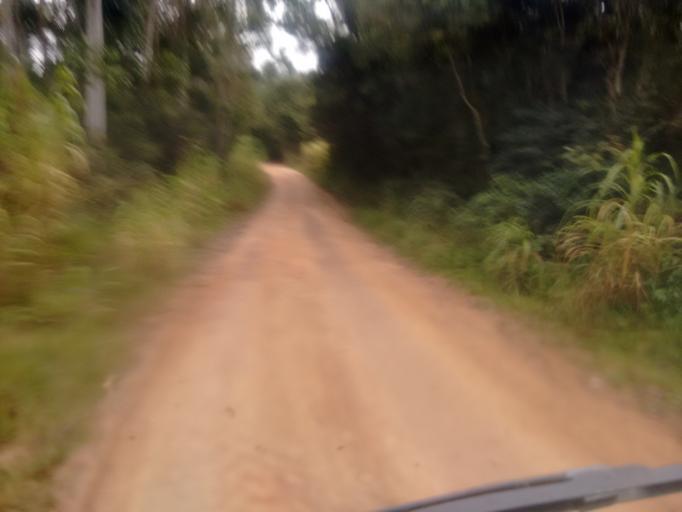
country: BR
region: Rio Grande do Sul
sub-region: Camaqua
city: Camaqua
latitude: -30.7230
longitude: -51.8639
